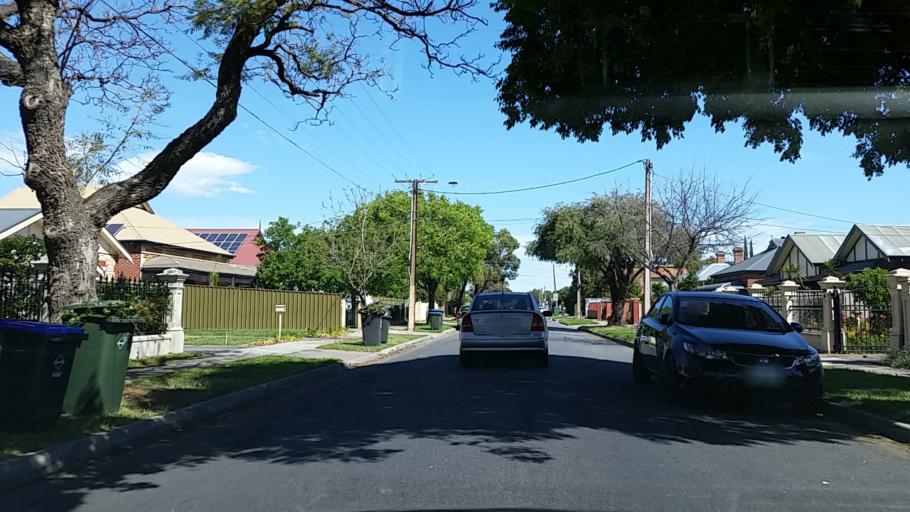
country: AU
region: South Australia
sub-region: Charles Sturt
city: Allenby Gardens
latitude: -34.9028
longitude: 138.5576
